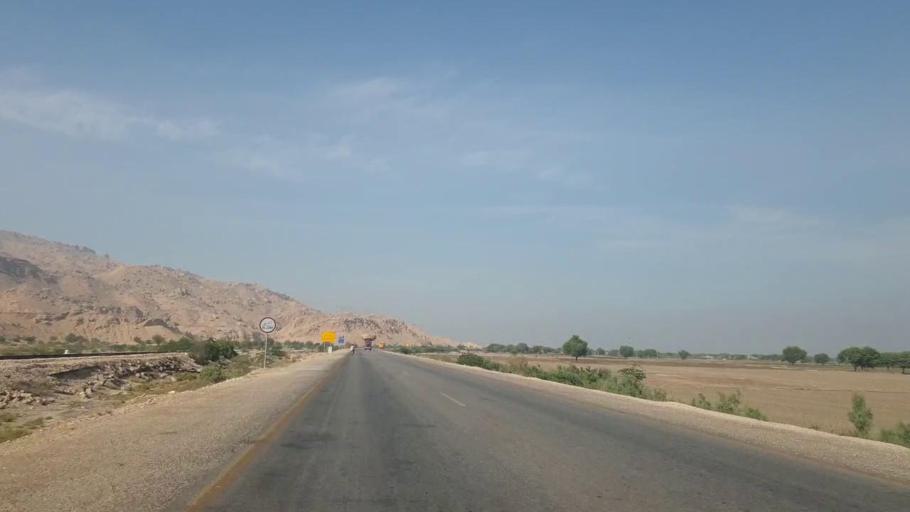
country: PK
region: Sindh
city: Sehwan
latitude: 26.2833
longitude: 67.8955
